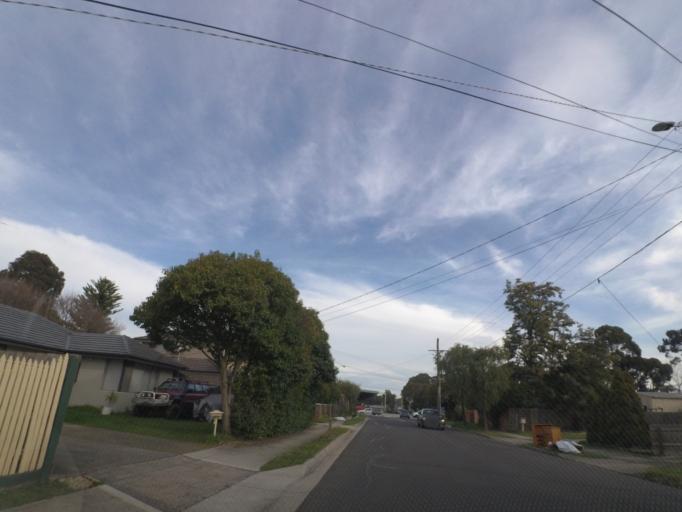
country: AU
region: Victoria
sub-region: Knox
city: Scoresby
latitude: -37.8972
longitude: 145.2405
